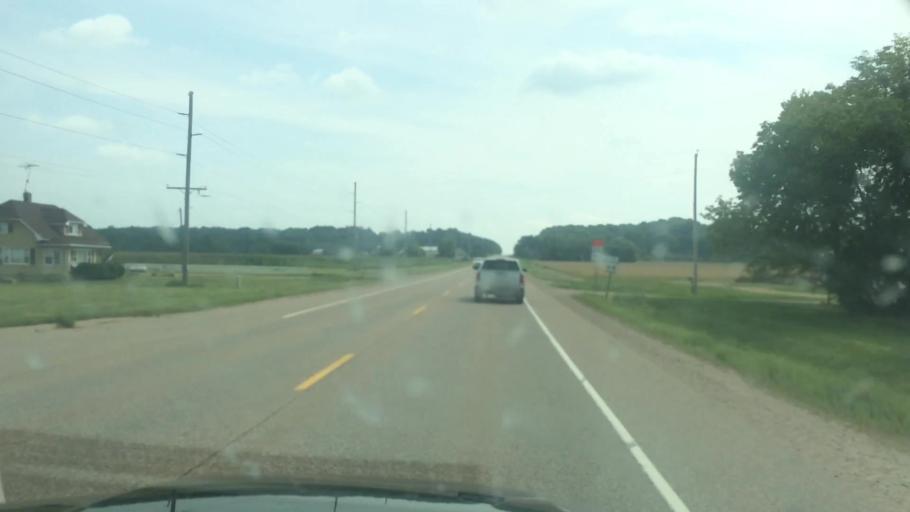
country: US
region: Wisconsin
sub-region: Langlade County
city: Antigo
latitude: 45.1621
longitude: -89.0727
